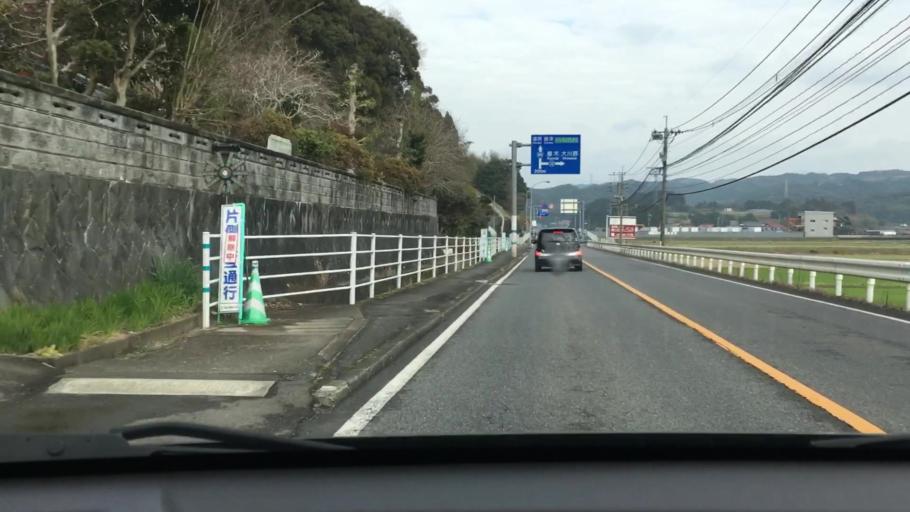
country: JP
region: Saga Prefecture
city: Imaricho-ko
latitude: 33.3047
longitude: 129.9234
